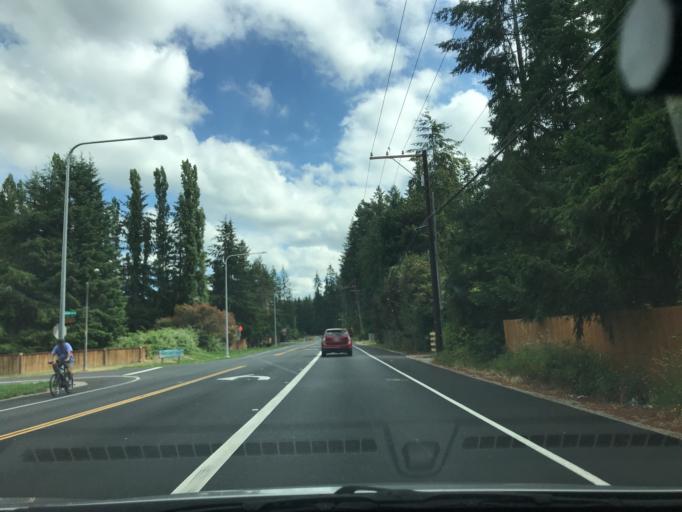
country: US
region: Washington
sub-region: King County
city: Lake Morton-Berrydale
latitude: 47.3039
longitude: -122.0867
